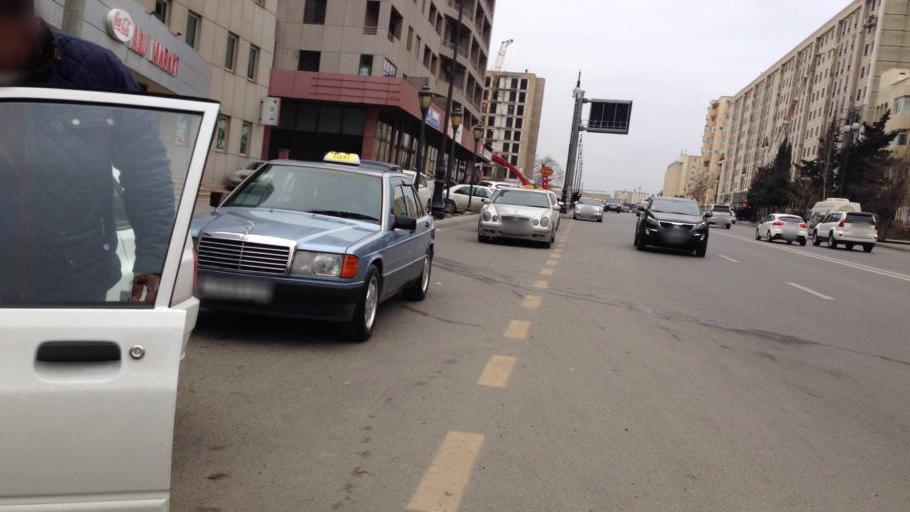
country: AZ
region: Baki
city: Baku
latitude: 40.3990
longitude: 49.8591
